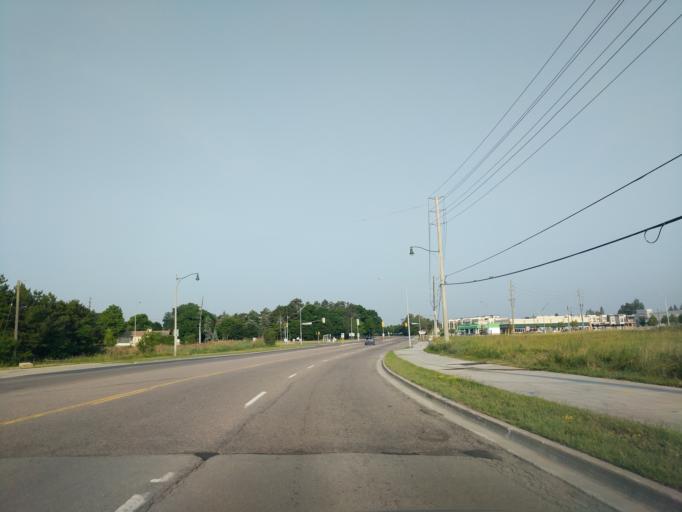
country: CA
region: Ontario
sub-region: York
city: Richmond Hill
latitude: 43.8937
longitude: -79.4178
